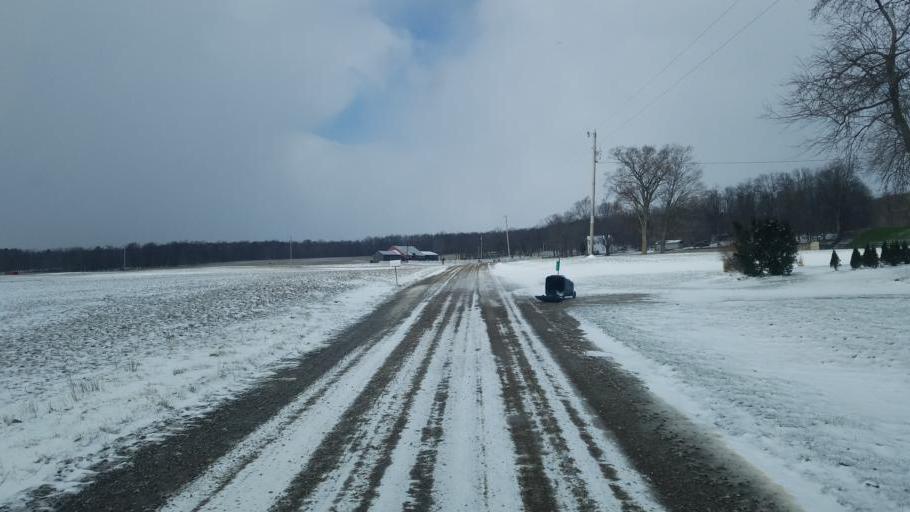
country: US
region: Ohio
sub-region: Richland County
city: Lexington
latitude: 40.6359
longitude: -82.6548
